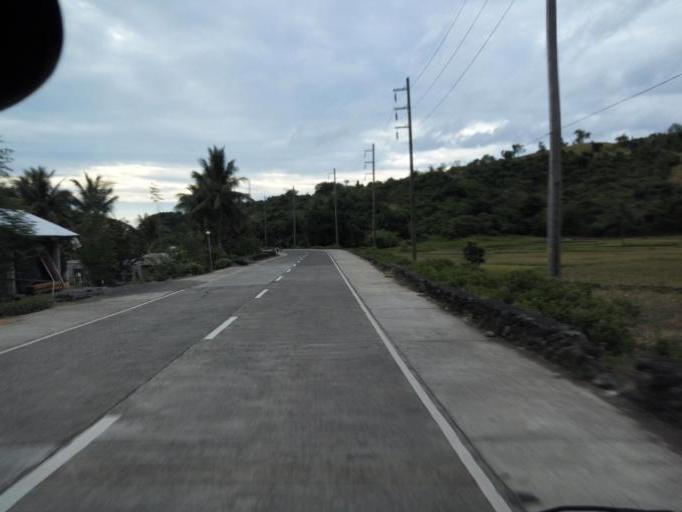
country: PH
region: Cagayan Valley
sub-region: Province of Cagayan
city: Casambalangan
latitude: 18.3932
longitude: 122.1379
